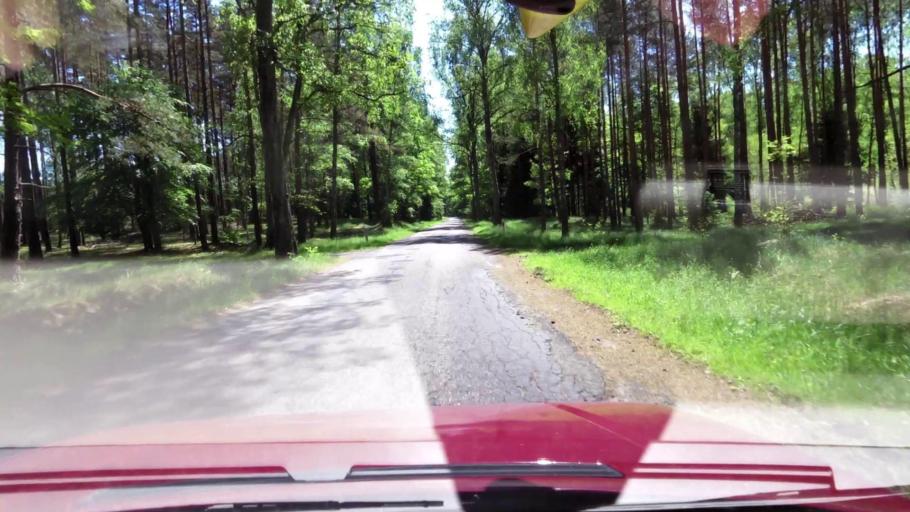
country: PL
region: West Pomeranian Voivodeship
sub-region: Powiat koszalinski
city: Bobolice
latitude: 54.0563
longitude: 16.5765
